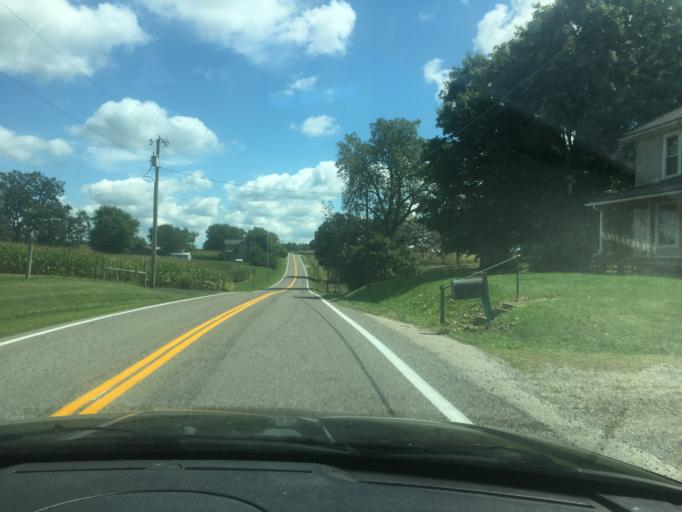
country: US
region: Ohio
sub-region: Logan County
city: West Liberty
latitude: 40.2331
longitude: -83.7192
